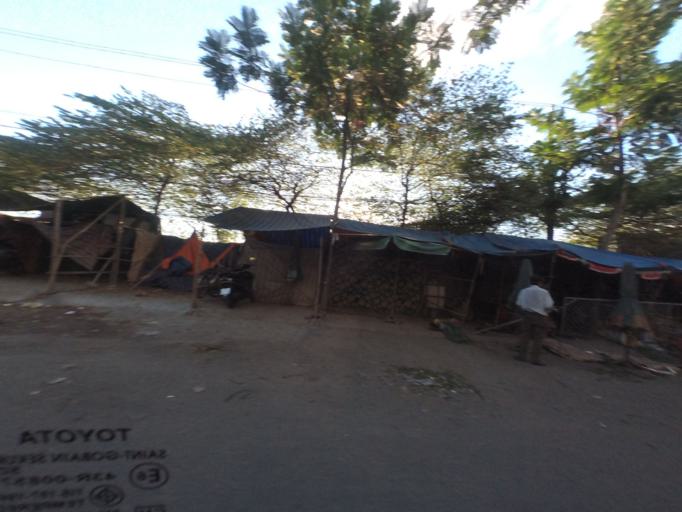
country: VN
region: Thua Thien-Hue
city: Hue
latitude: 16.4918
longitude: 107.5835
